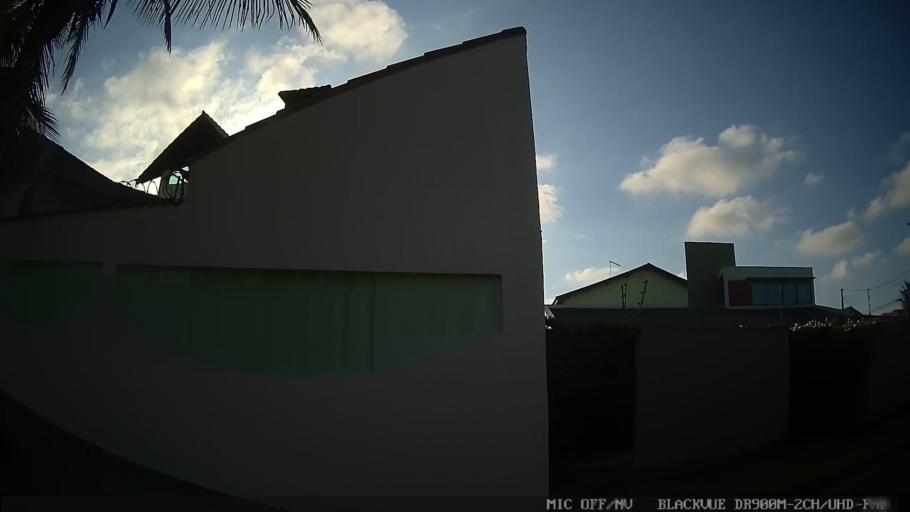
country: BR
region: Sao Paulo
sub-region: Peruibe
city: Peruibe
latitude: -24.2967
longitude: -46.9666
